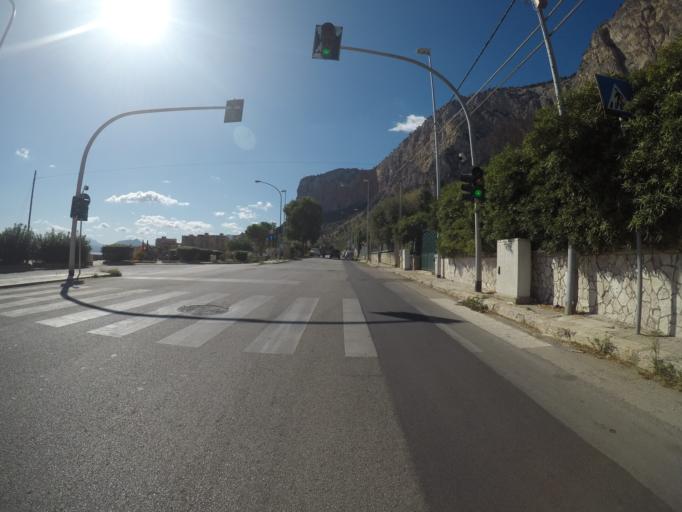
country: IT
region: Sicily
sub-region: Palermo
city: Palermo
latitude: 38.1693
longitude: 13.3666
